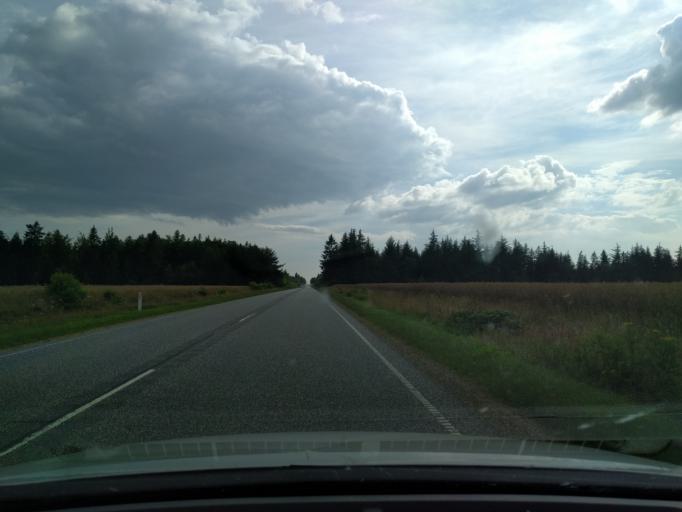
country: DK
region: Central Jutland
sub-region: Herning Kommune
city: Kibaek
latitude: 56.0674
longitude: 8.9026
